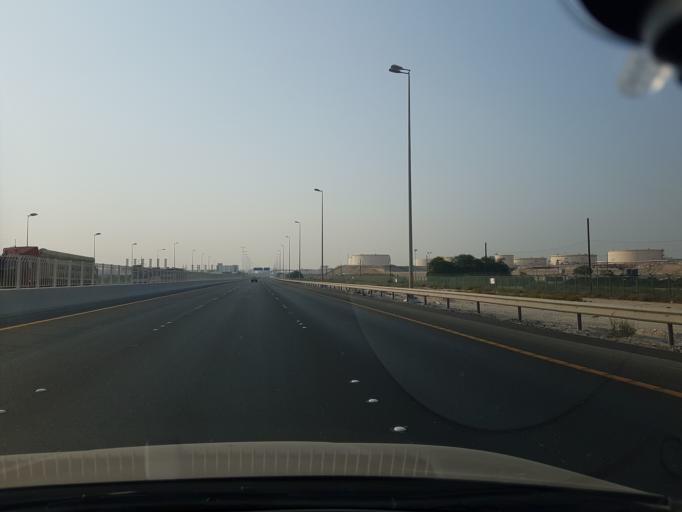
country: BH
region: Northern
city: Ar Rifa'
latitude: 26.1090
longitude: 50.5990
